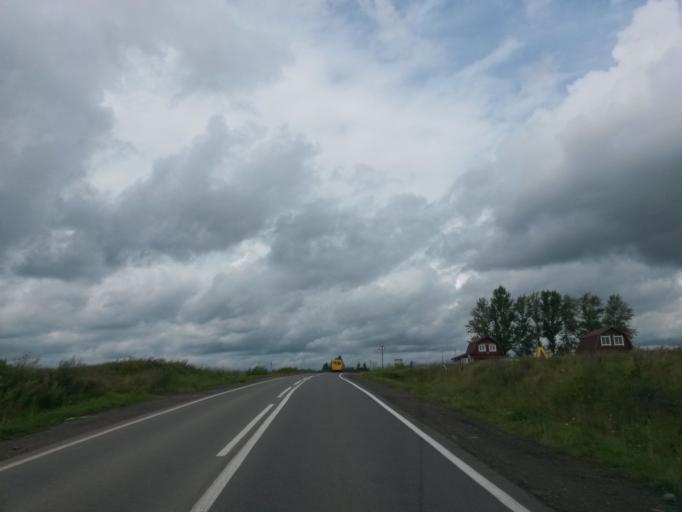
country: RU
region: Jaroslavl
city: Yaroslavl
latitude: 57.7882
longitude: 39.8342
